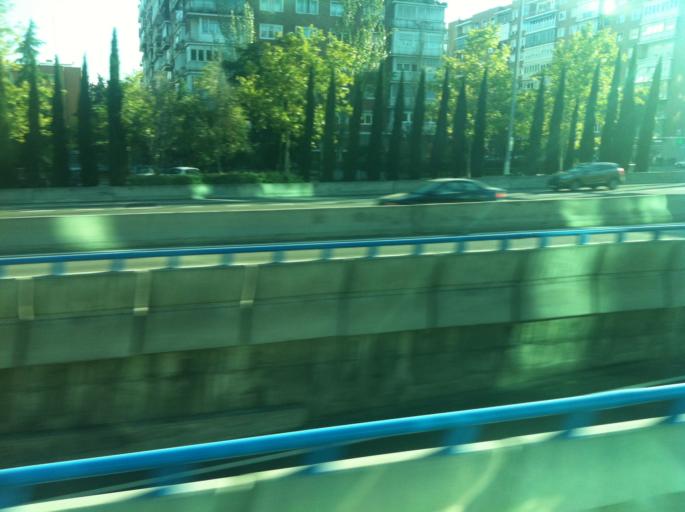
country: ES
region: Madrid
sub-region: Provincia de Madrid
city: Ciudad Lineal
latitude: 40.4437
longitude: -3.6636
